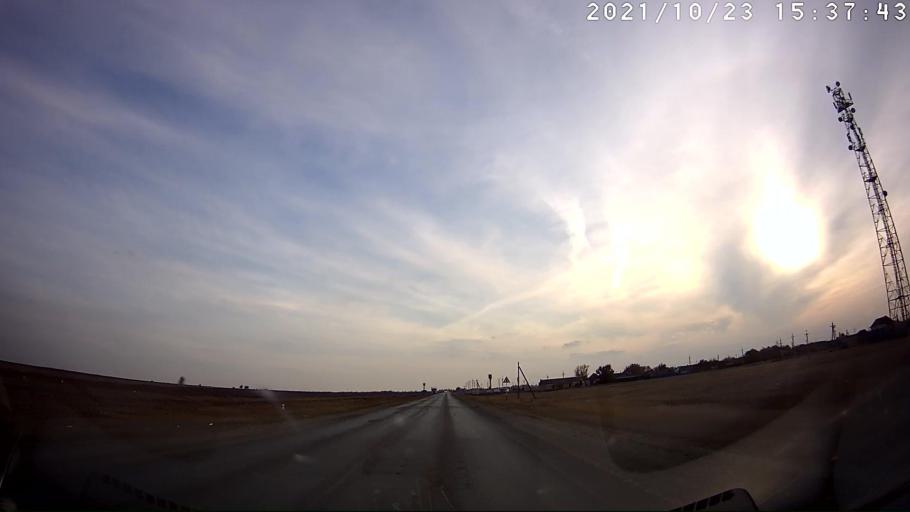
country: RU
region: Volgograd
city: Bereslavka
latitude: 48.1418
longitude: 44.1224
